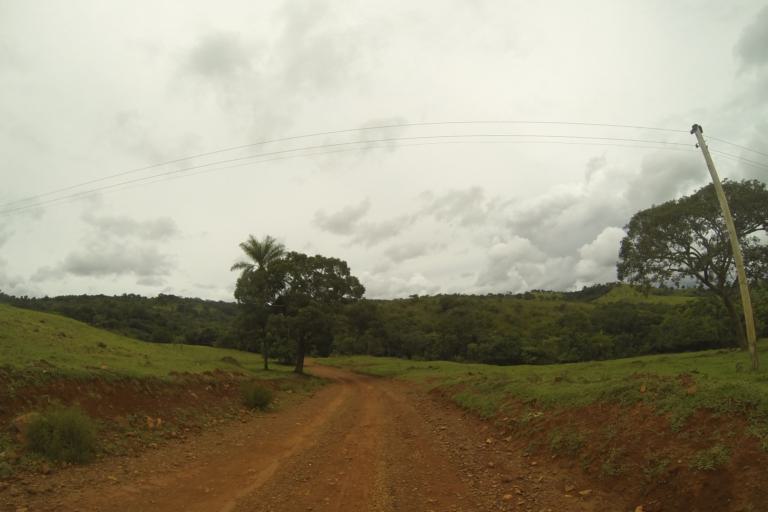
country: BR
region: Minas Gerais
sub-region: Ibia
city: Ibia
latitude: -19.6553
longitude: -46.7000
